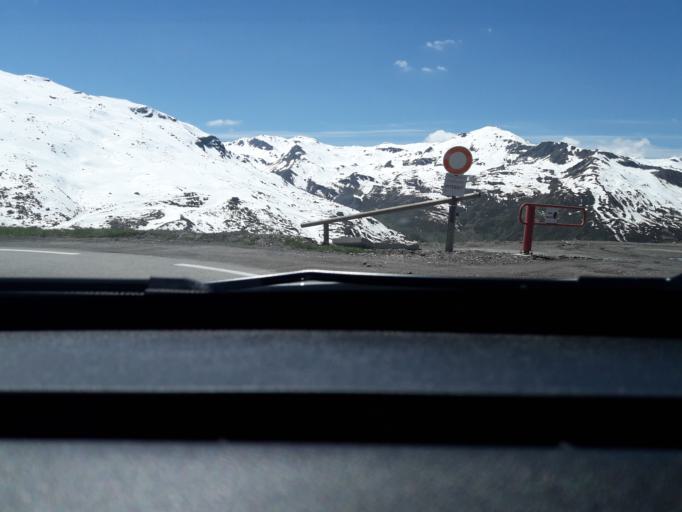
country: FR
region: Rhone-Alpes
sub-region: Departement de la Savoie
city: Val Thorens
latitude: 45.3013
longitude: 6.5690
